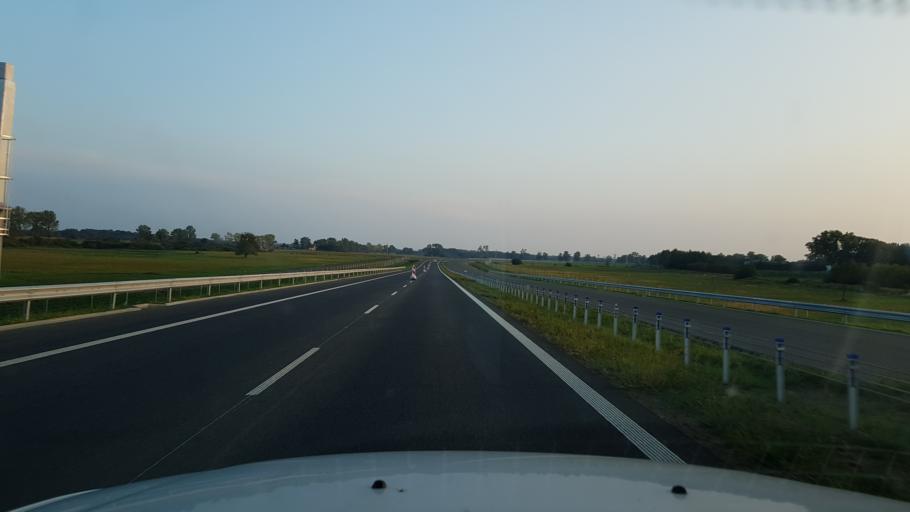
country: PL
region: West Pomeranian Voivodeship
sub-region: Powiat goleniowski
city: Nowogard
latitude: 53.7235
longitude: 15.1974
